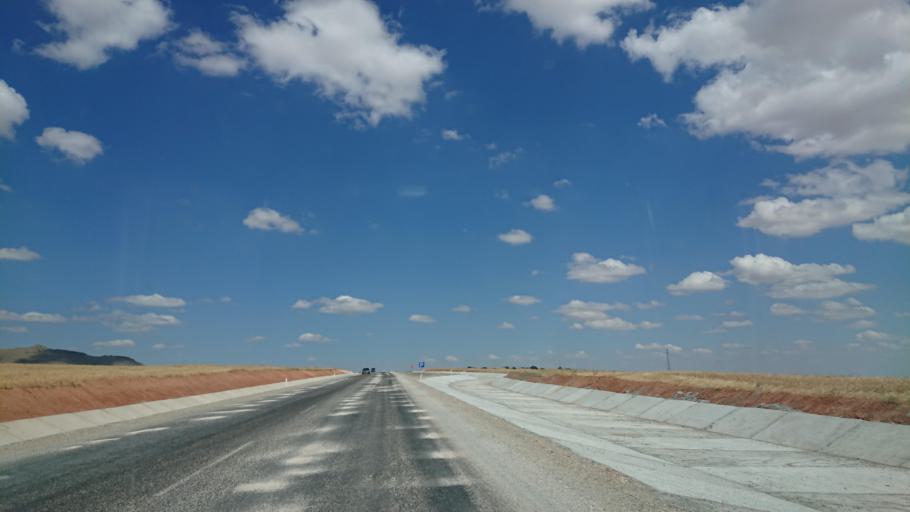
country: TR
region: Kirsehir
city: Kirsehir
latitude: 39.1238
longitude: 33.9753
